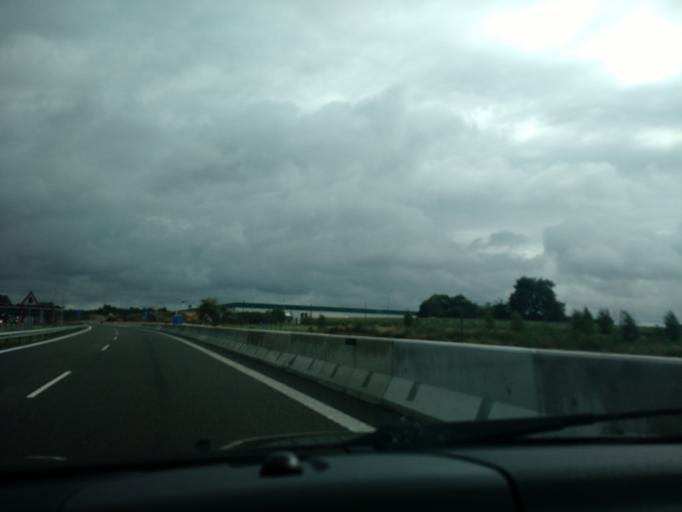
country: ES
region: Galicia
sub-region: Provincia da Coruna
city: Oroso
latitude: 42.9761
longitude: -8.4416
